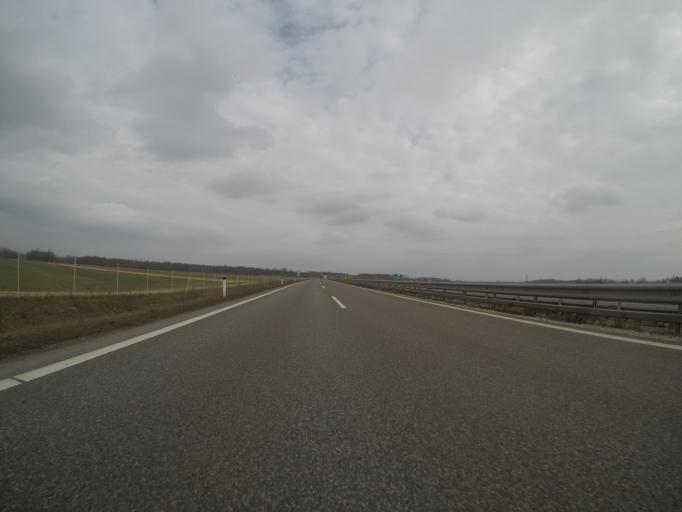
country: SI
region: Beltinci
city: Gancani
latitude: 46.6398
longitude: 16.2514
